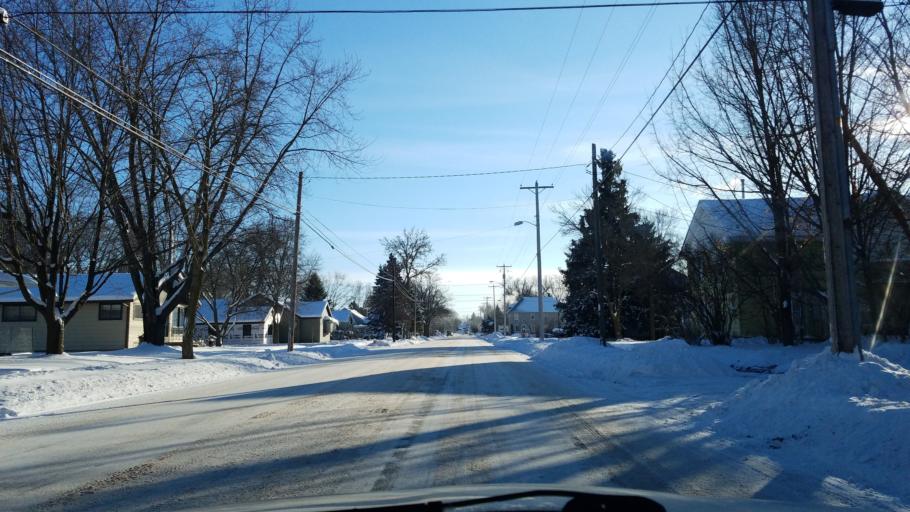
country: US
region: Wisconsin
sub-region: Barron County
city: Rice Lake
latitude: 45.5067
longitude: -91.7415
